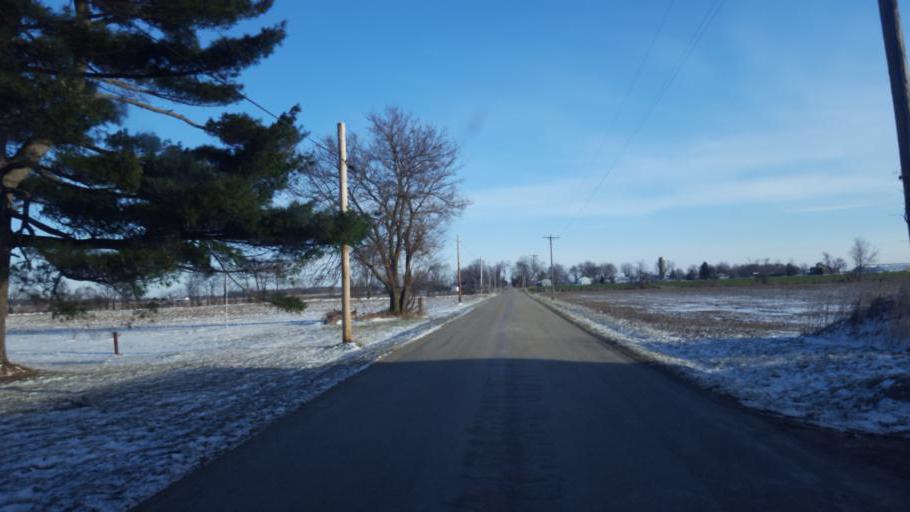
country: US
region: Ohio
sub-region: Morrow County
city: Cardington
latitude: 40.5811
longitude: -82.9188
